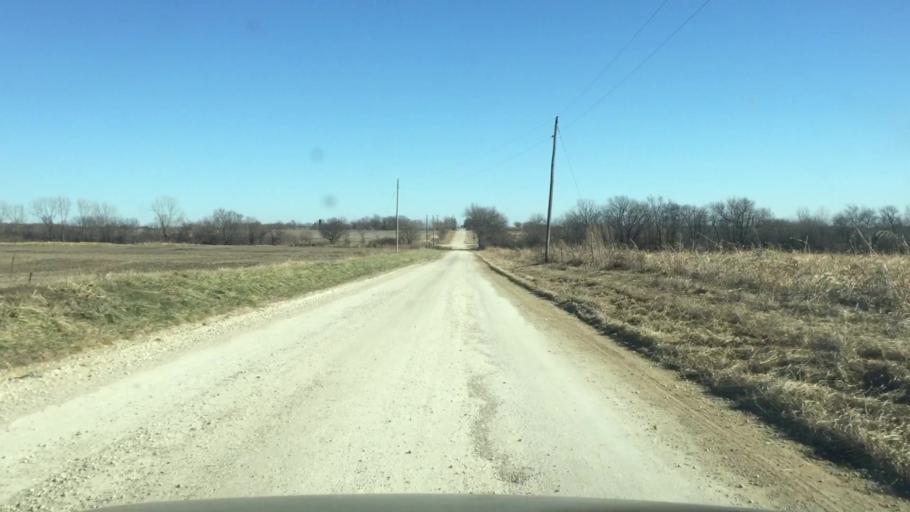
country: US
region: Kansas
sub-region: Allen County
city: Humboldt
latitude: 37.8494
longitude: -95.3946
